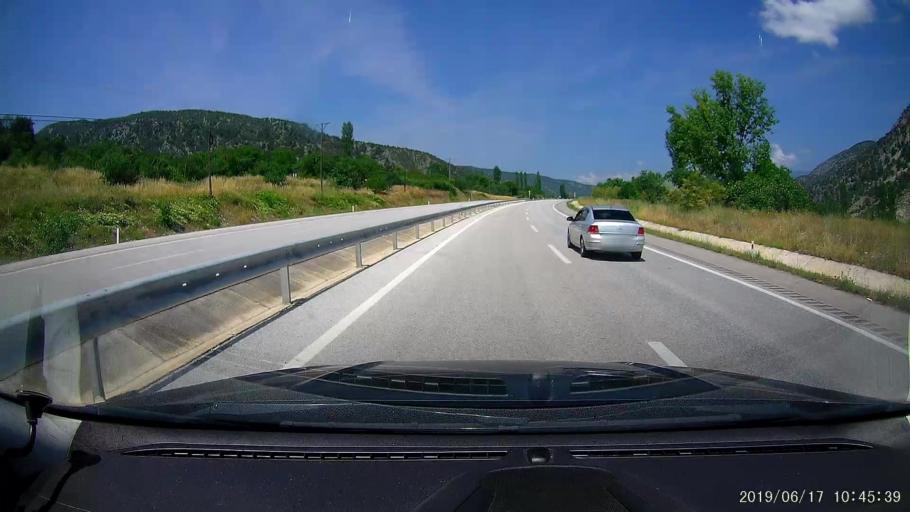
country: TR
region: Corum
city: Hacihamza
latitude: 41.0624
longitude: 34.4822
